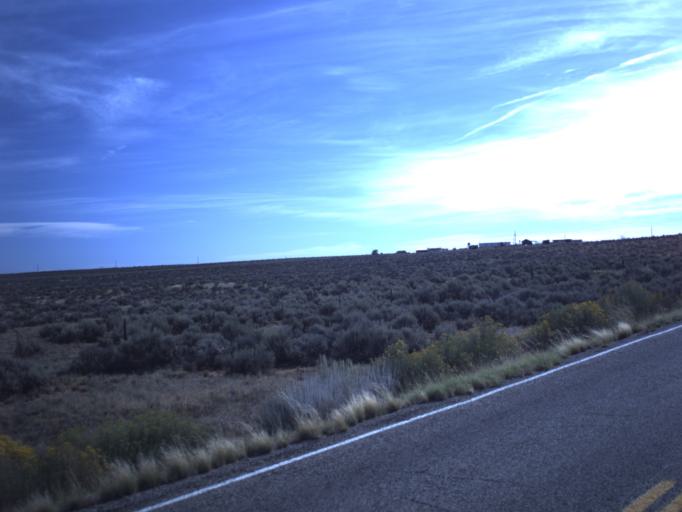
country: US
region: Utah
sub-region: San Juan County
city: Blanding
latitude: 37.4238
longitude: -109.3430
